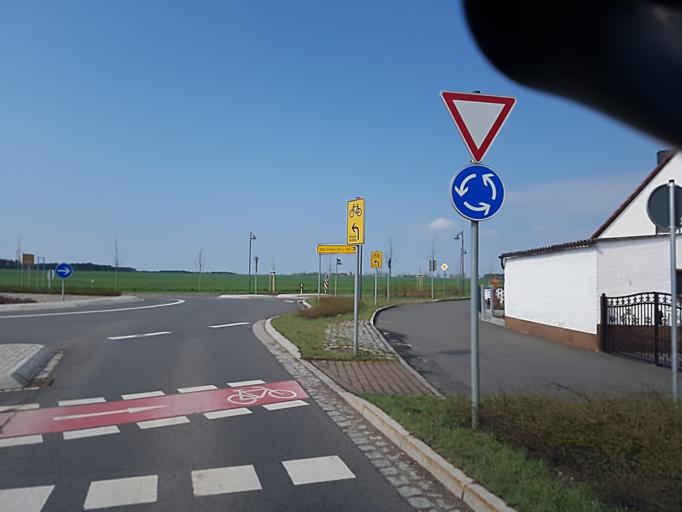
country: DE
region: Saxony
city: Zinna
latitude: 51.5639
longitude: 12.9228
